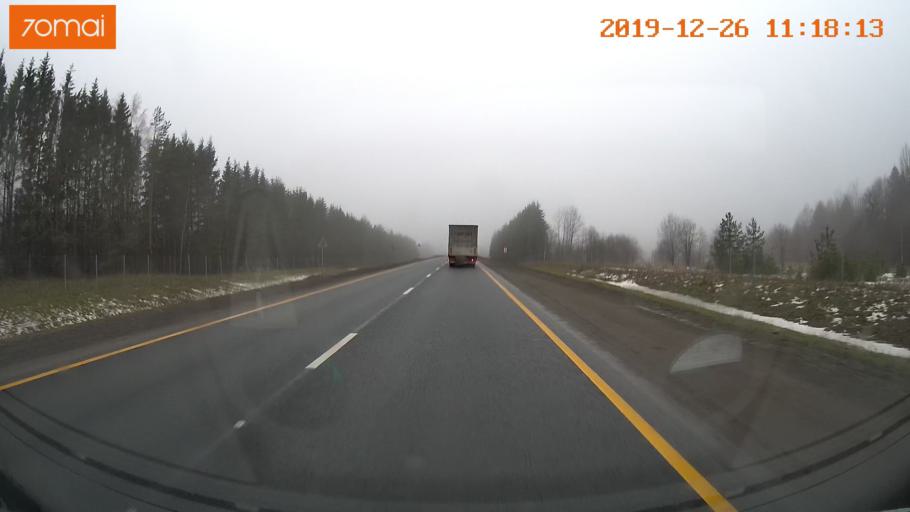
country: RU
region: Vologda
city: Chebsara
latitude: 59.1193
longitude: 39.0393
